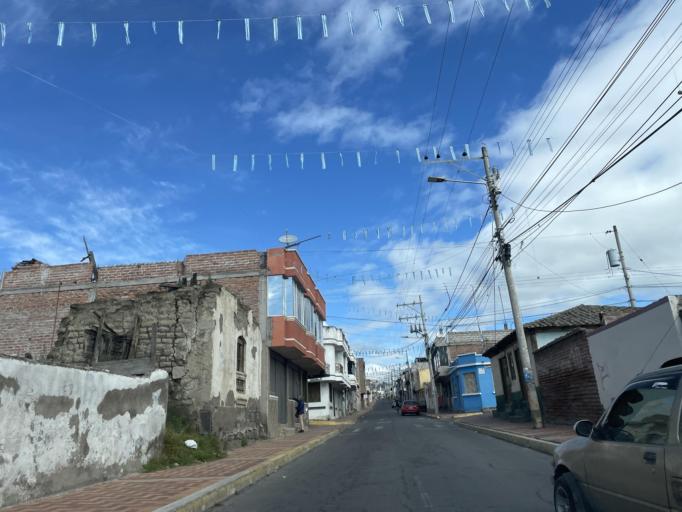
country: EC
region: Chimborazo
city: Guano
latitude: -1.6078
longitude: -78.6354
